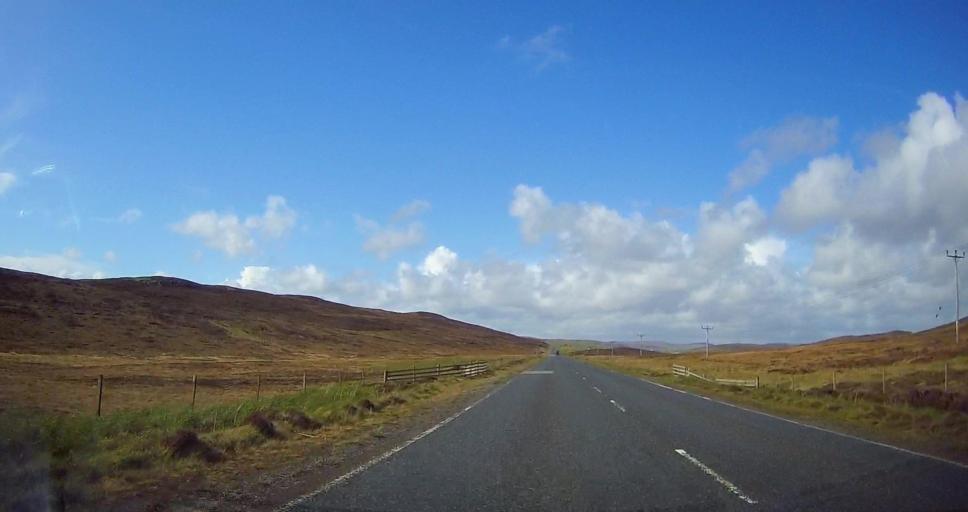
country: GB
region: Scotland
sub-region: Shetland Islands
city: Lerwick
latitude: 60.2060
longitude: -1.2333
